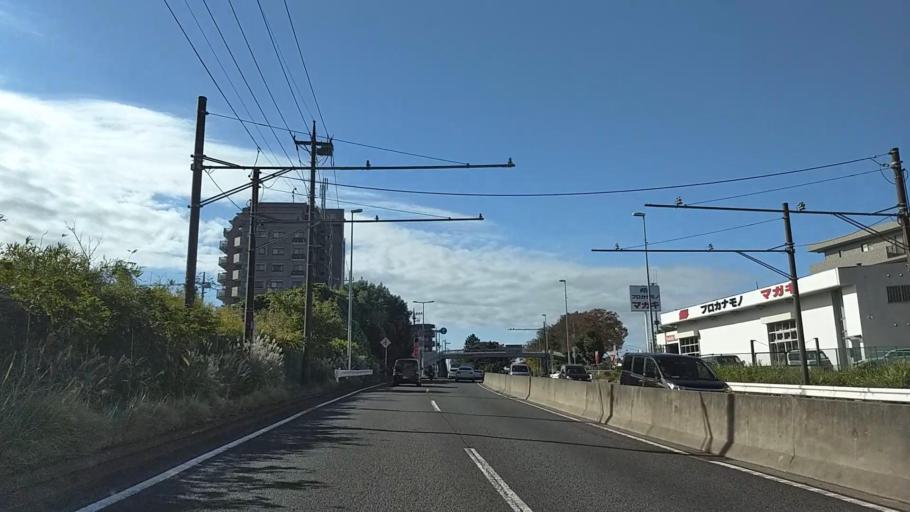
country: JP
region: Kanagawa
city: Fujisawa
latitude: 35.3888
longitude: 139.5201
